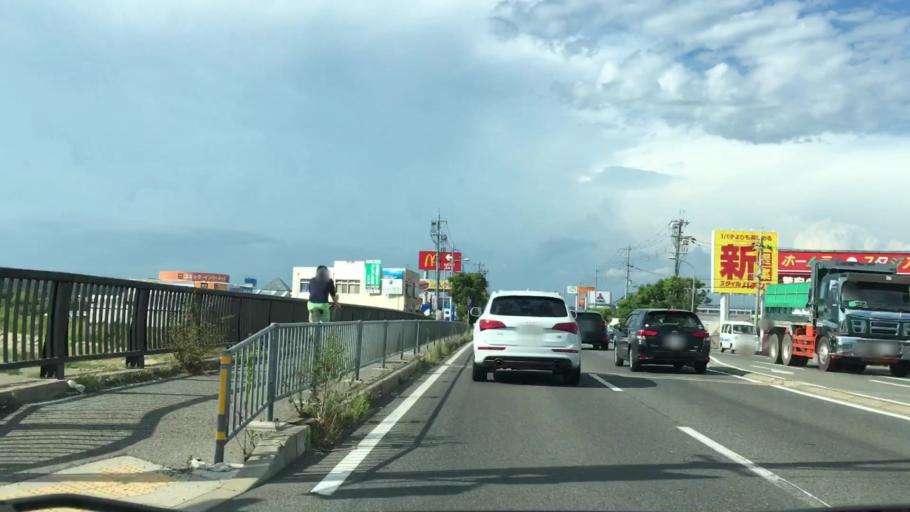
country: JP
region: Hyogo
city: Akashi
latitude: 34.6778
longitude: 134.9819
